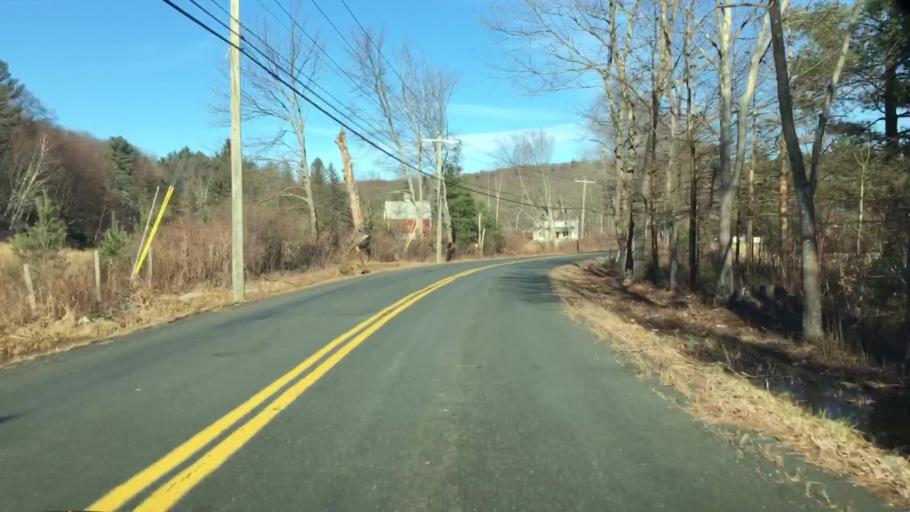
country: US
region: Connecticut
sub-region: Tolland County
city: Crystal Lake
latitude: 41.9294
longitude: -72.3882
